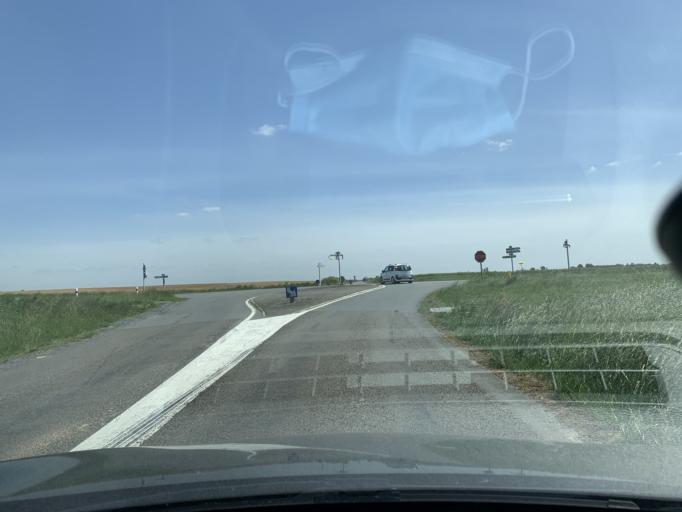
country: FR
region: Nord-Pas-de-Calais
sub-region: Departement du Nord
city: Rumilly-en-Cambresis
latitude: 50.1362
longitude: 3.1988
